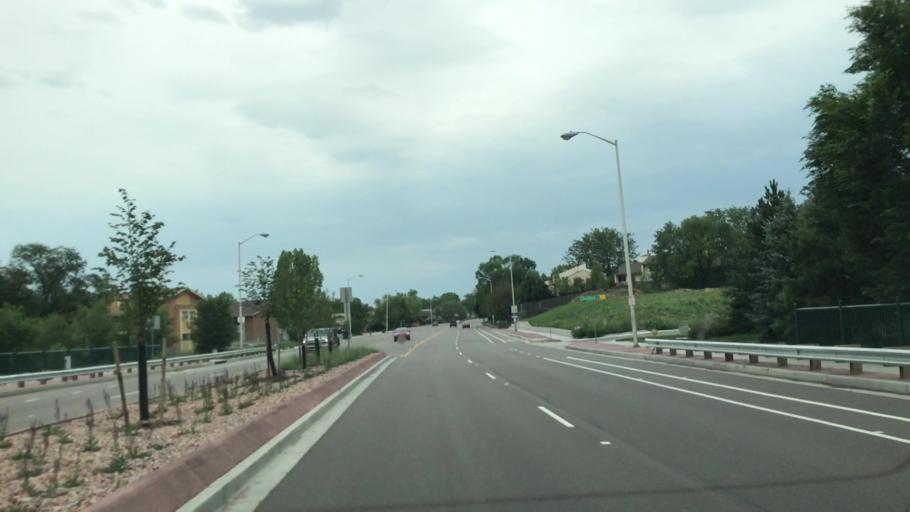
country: US
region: Colorado
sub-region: El Paso County
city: Colorado Springs
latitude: 38.8906
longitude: -104.8492
